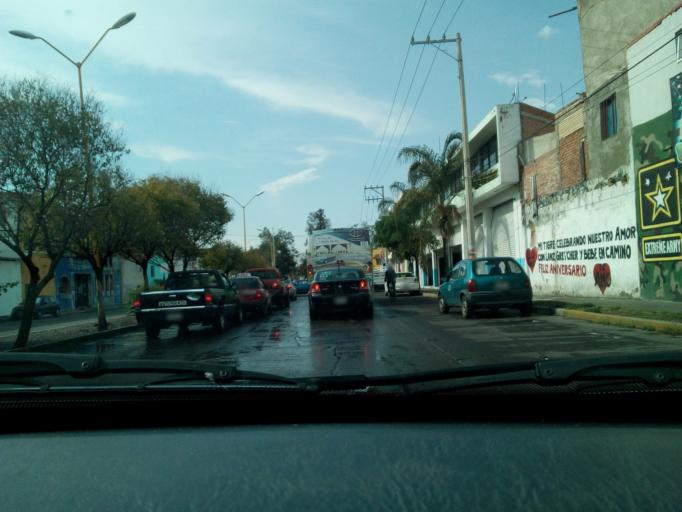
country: MX
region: Aguascalientes
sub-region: Aguascalientes
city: Aguascalientes
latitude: 21.8904
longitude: -102.2950
